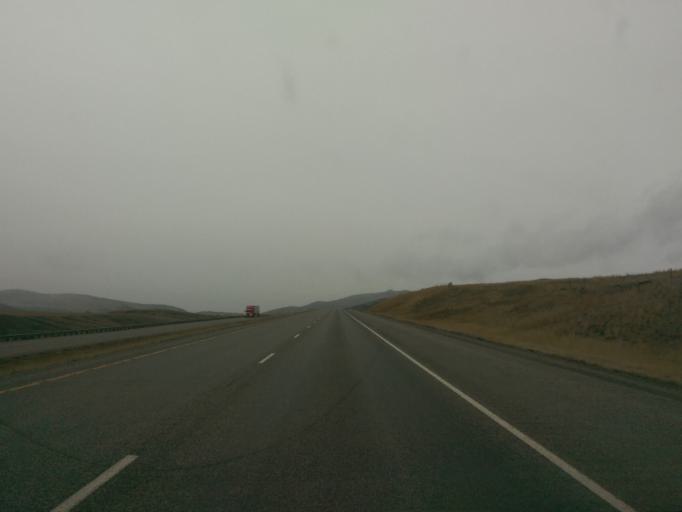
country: US
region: Montana
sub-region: Gallatin County
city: Three Forks
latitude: 45.9107
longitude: -111.7812
